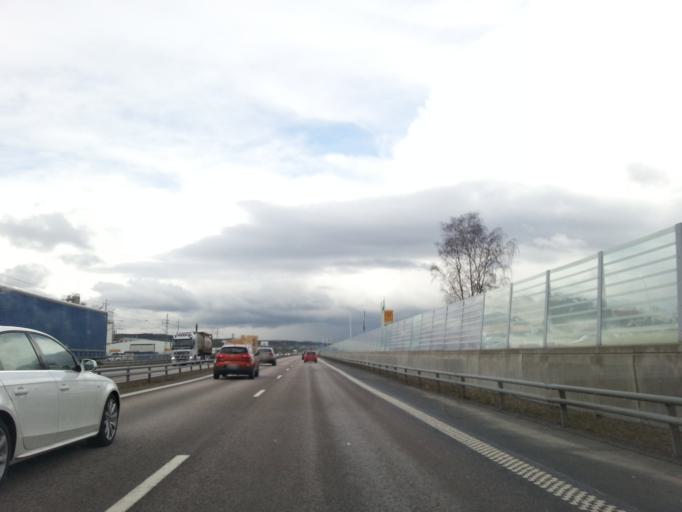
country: SE
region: Vaestra Goetaland
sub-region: Ale Kommun
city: Surte
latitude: 57.8448
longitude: 12.0136
